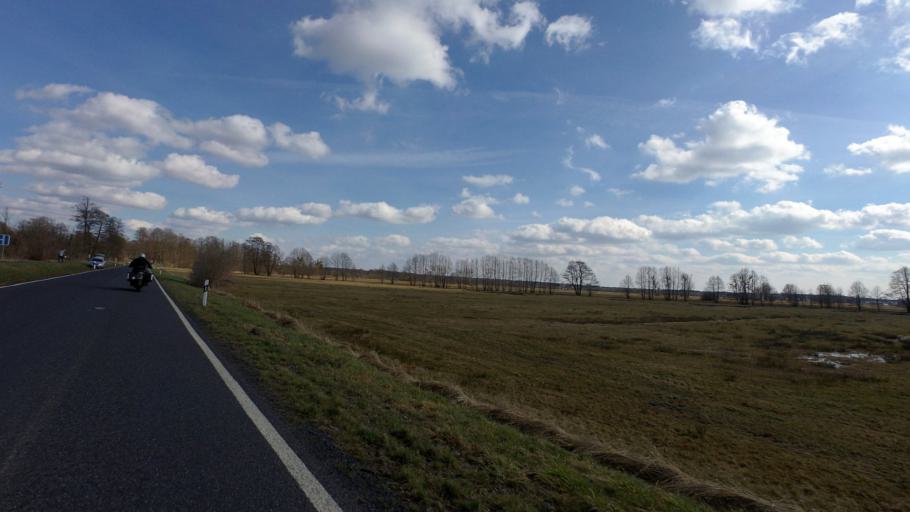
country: DE
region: Brandenburg
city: Marienwerder
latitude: 52.8397
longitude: 13.5610
